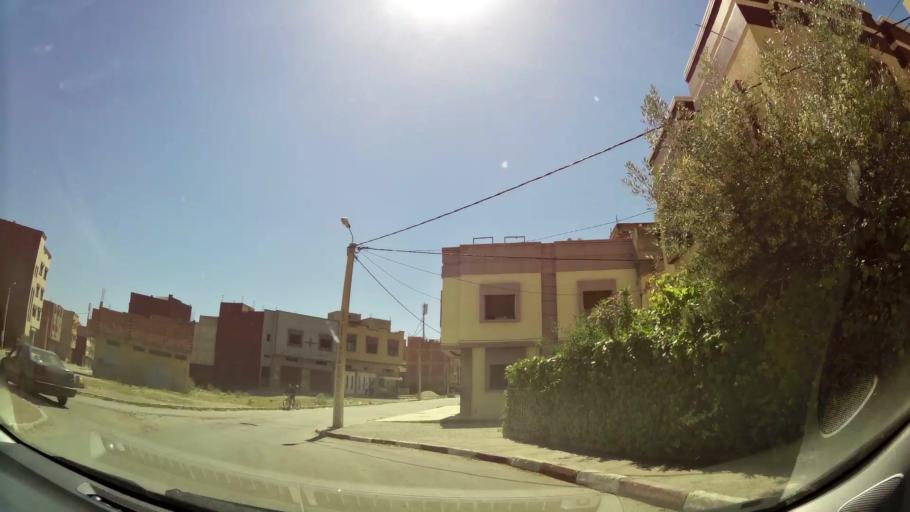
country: MA
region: Oriental
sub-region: Oujda-Angad
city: Oujda
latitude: 34.6573
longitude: -1.8759
